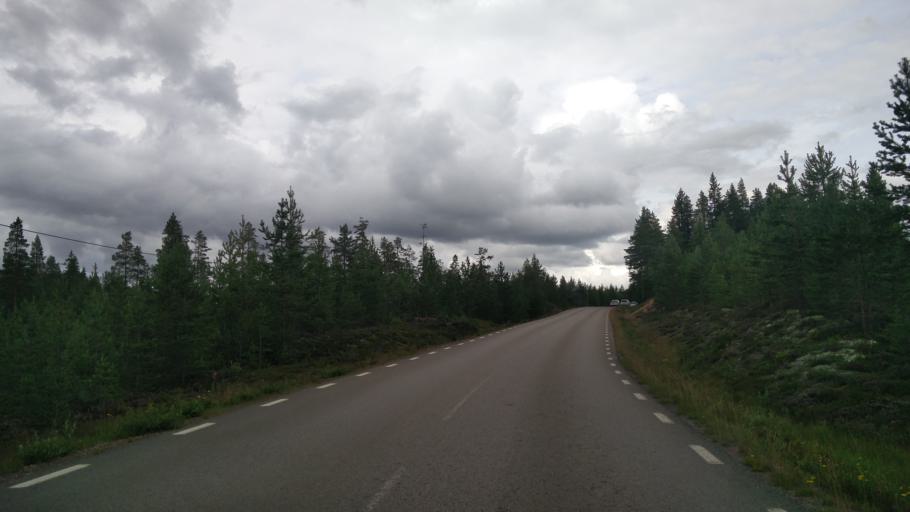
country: NO
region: Hedmark
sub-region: Trysil
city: Innbygda
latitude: 61.1569
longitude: 12.8153
